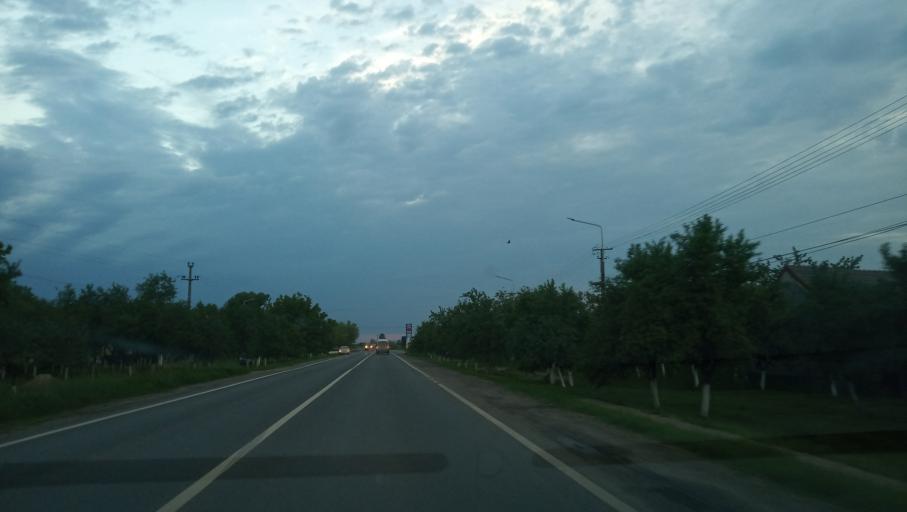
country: RO
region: Timis
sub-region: Comuna Jebel
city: Jebel
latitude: 45.5689
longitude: 21.2074
